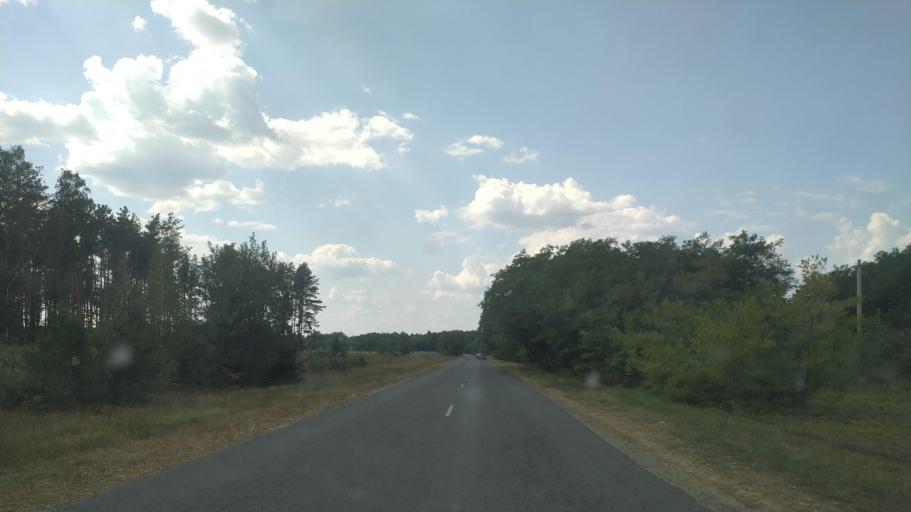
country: BY
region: Brest
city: Drahichyn
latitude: 52.1031
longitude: 25.1336
